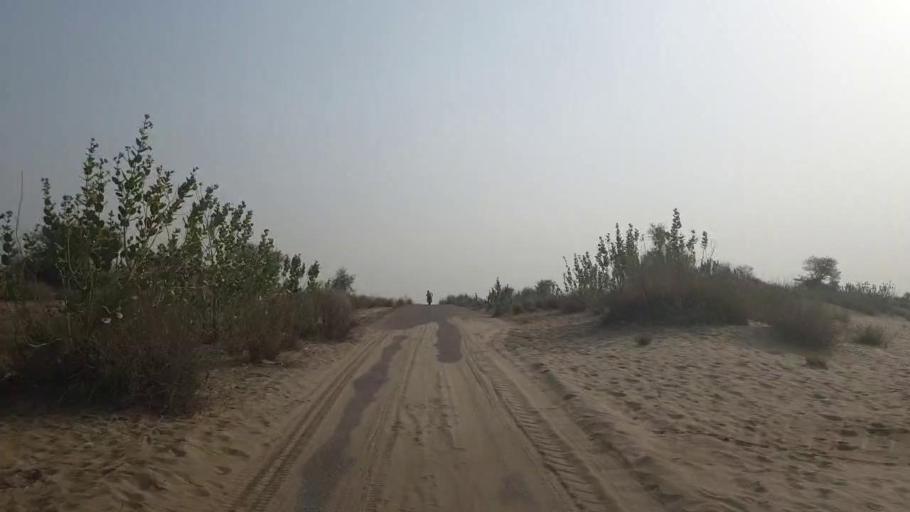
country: PK
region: Sindh
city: Chor
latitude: 25.4608
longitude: 69.9662
